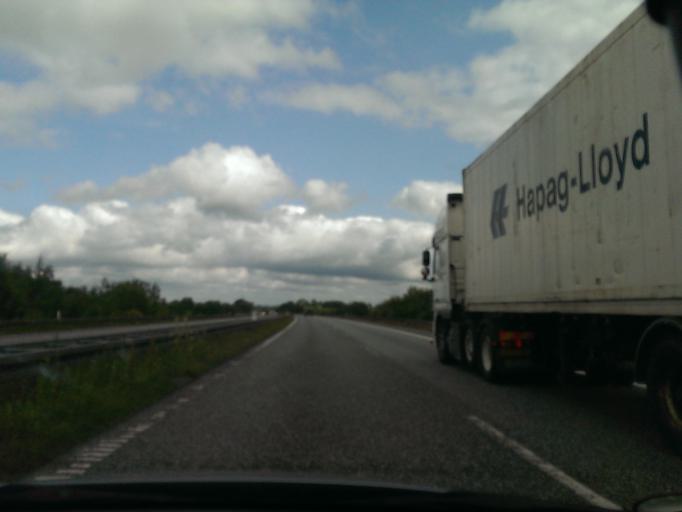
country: DK
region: North Denmark
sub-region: Mariagerfjord Kommune
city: Hobro
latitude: 56.6781
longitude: 9.7330
